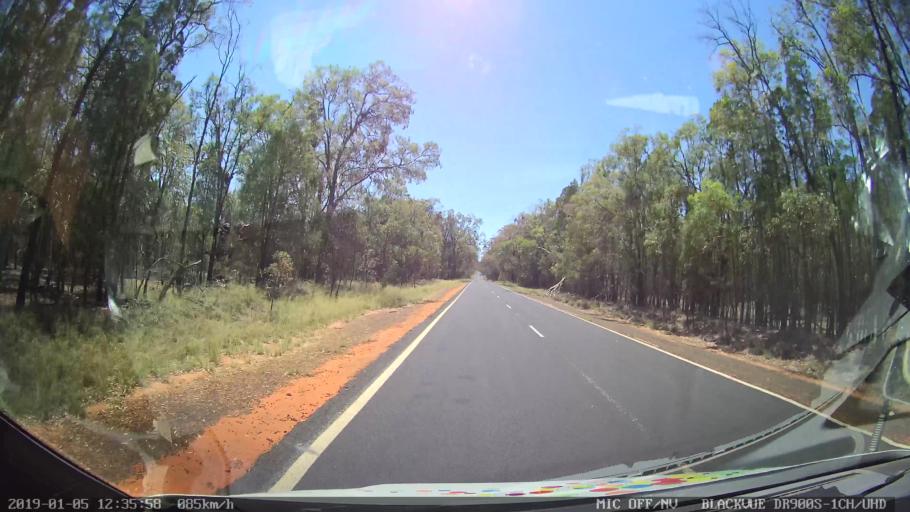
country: AU
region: New South Wales
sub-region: Warrumbungle Shire
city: Coonabarabran
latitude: -31.2083
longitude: 149.4333
